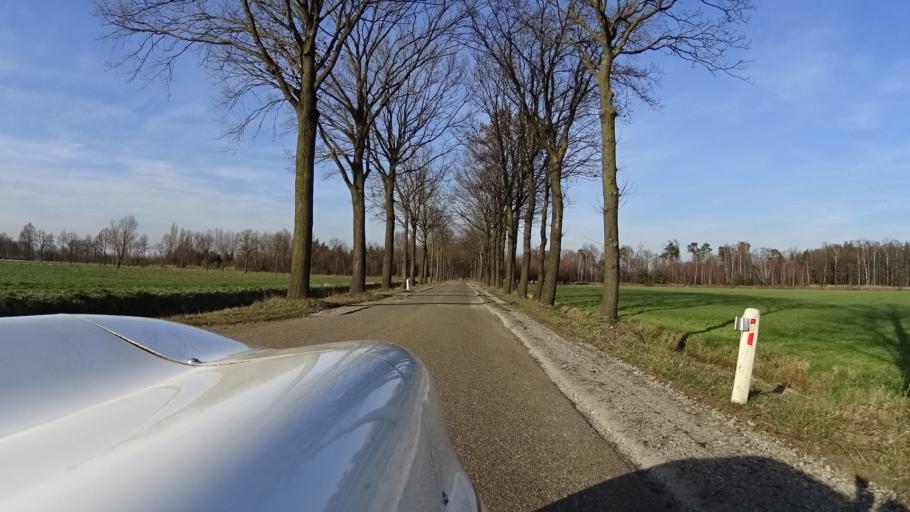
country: NL
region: North Brabant
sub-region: Gemeente Veghel
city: Erp
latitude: 51.5757
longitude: 5.6253
